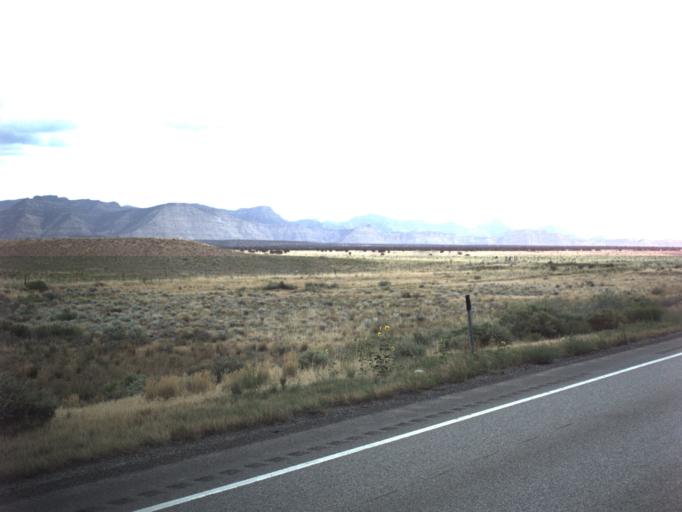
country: US
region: Utah
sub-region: Carbon County
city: East Carbon City
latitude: 39.4408
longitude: -110.4639
